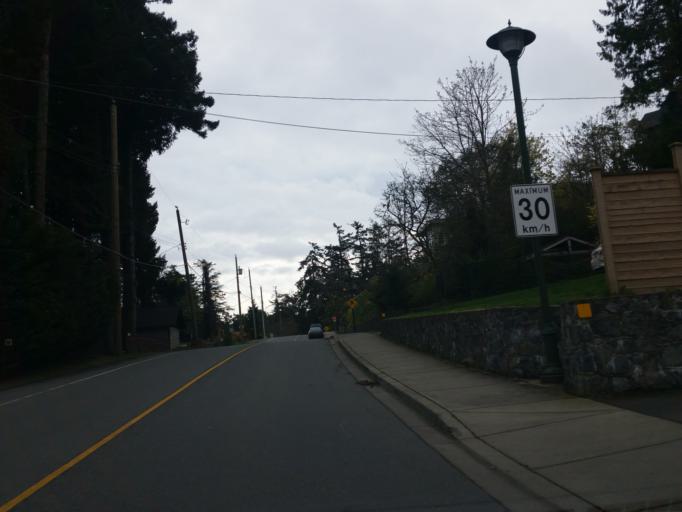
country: CA
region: British Columbia
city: Colwood
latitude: 48.4550
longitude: -123.4594
